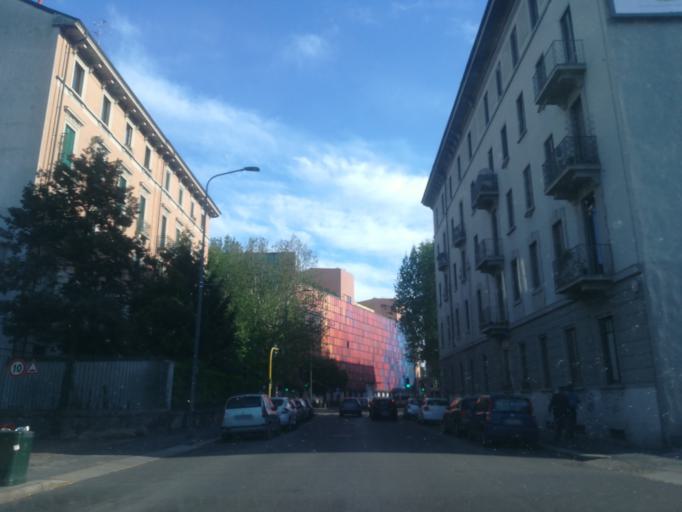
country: IT
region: Lombardy
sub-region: Citta metropolitana di Milano
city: Milano
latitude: 45.4978
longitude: 9.1817
